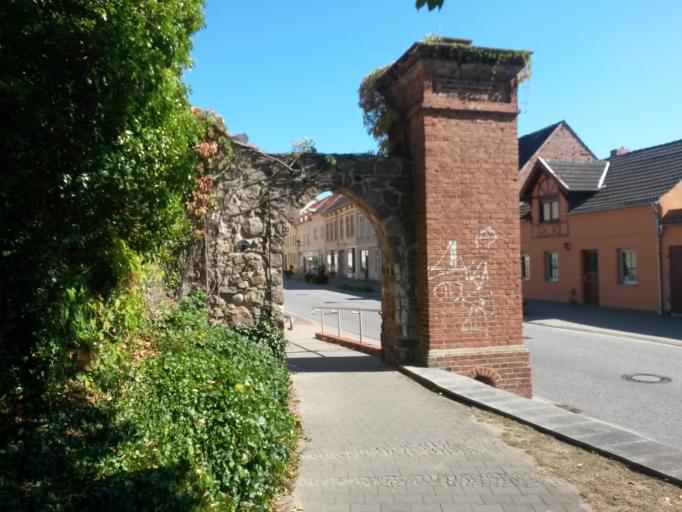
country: DE
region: Brandenburg
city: Lychen
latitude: 53.2106
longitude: 13.3116
